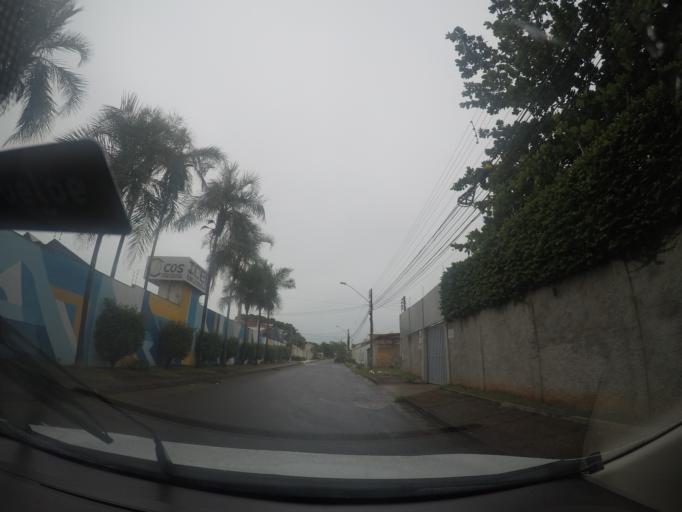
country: BR
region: Goias
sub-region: Goiania
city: Goiania
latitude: -16.6396
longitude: -49.2378
